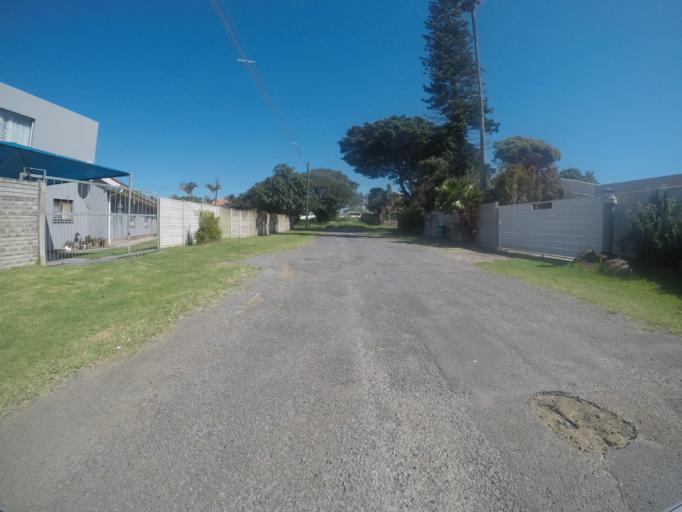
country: ZA
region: Eastern Cape
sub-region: Buffalo City Metropolitan Municipality
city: East London
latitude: -32.9455
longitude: 28.0047
